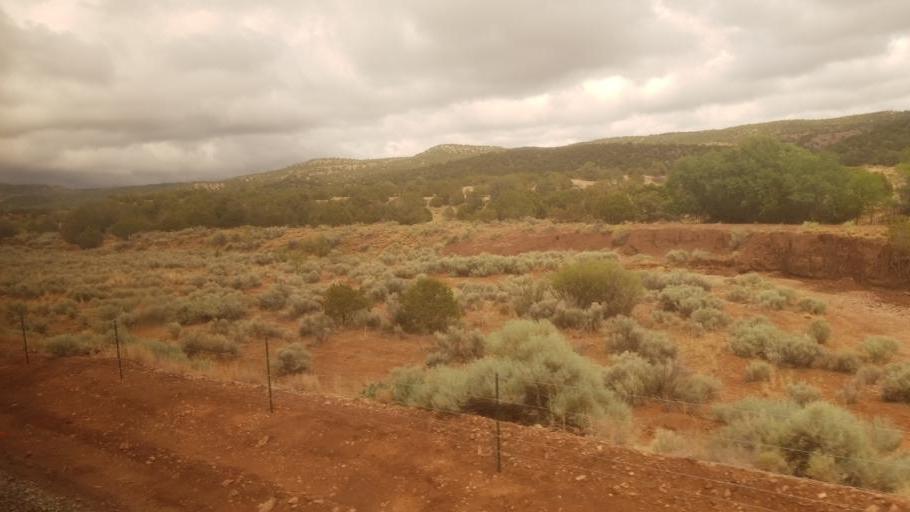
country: US
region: New Mexico
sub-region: Santa Fe County
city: Eldorado at Santa Fe
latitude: 35.4864
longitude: -105.8736
